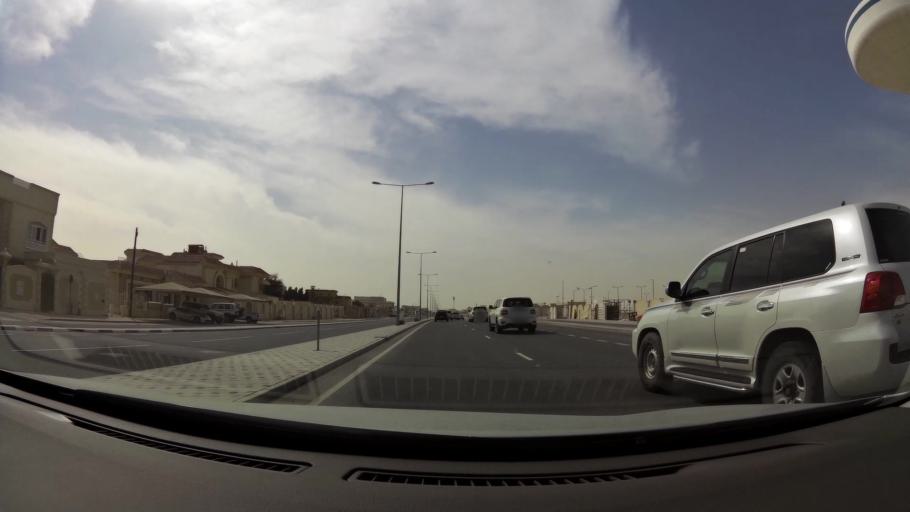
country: QA
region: Baladiyat ar Rayyan
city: Ar Rayyan
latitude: 25.3200
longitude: 51.4037
